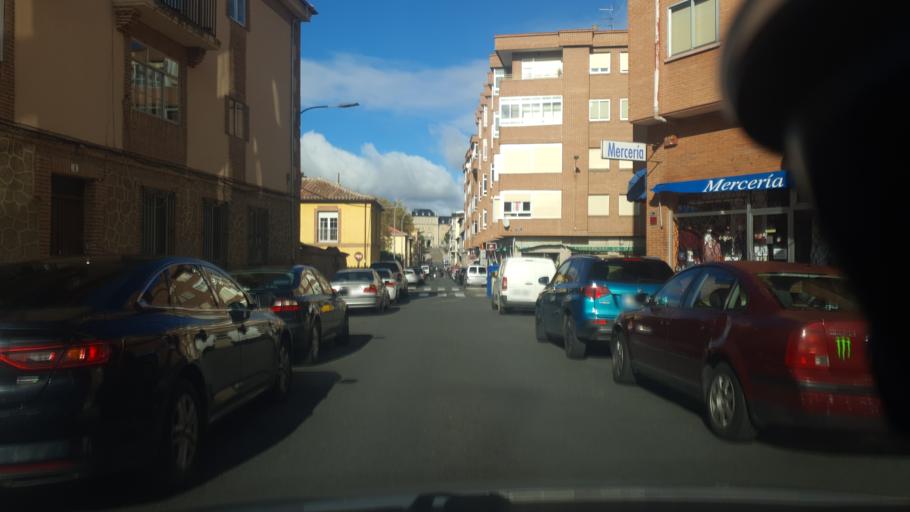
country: ES
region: Castille and Leon
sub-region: Provincia de Avila
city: Avila
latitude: 40.6588
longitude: -4.6886
